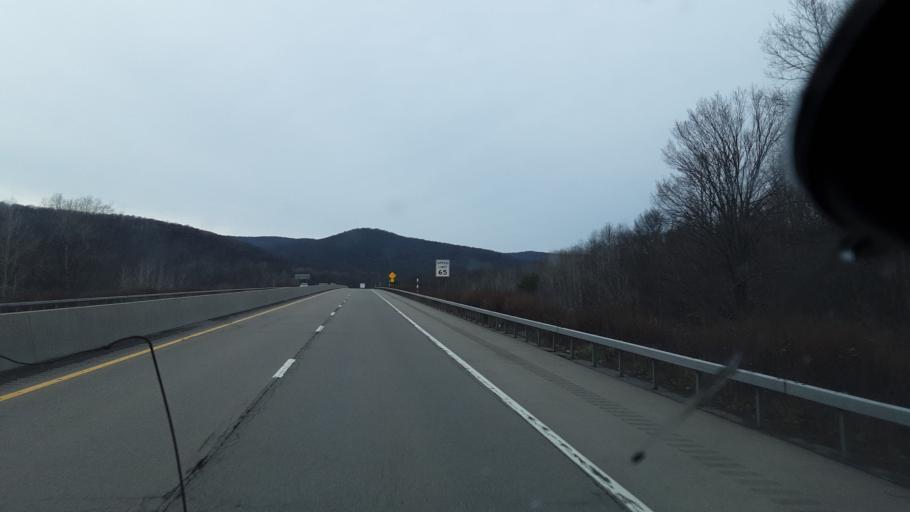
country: US
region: New York
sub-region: Cattaraugus County
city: Salamanca
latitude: 42.0904
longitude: -78.6406
